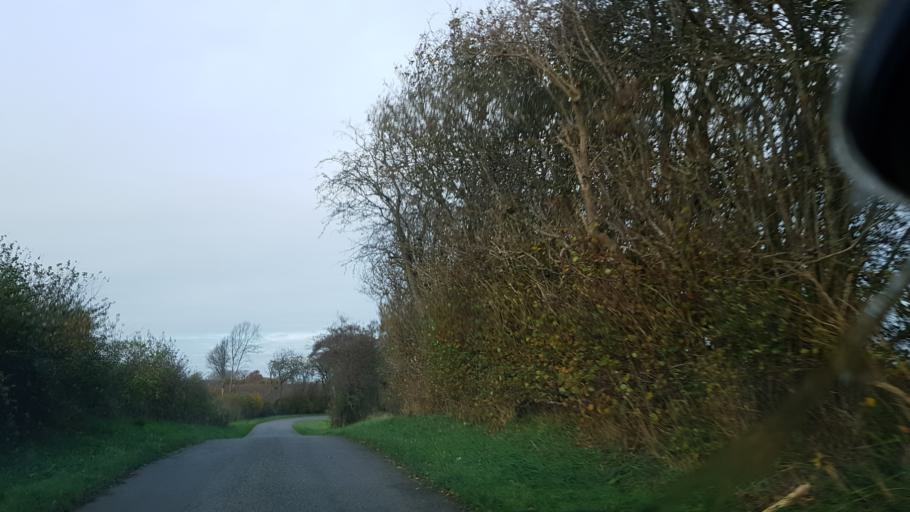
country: DK
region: South Denmark
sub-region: Haderslev Kommune
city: Vojens
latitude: 55.3223
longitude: 9.3693
